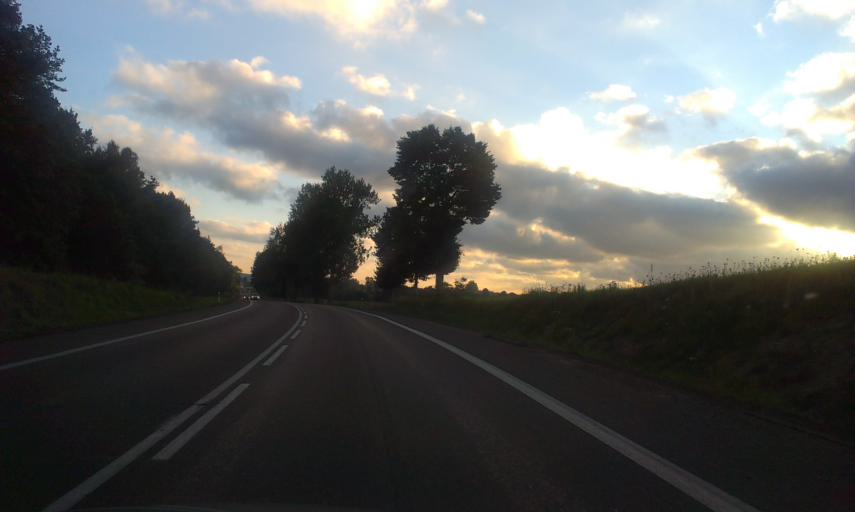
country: PL
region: West Pomeranian Voivodeship
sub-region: Powiat koszalinski
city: Sianow
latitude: 54.2538
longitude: 16.3637
